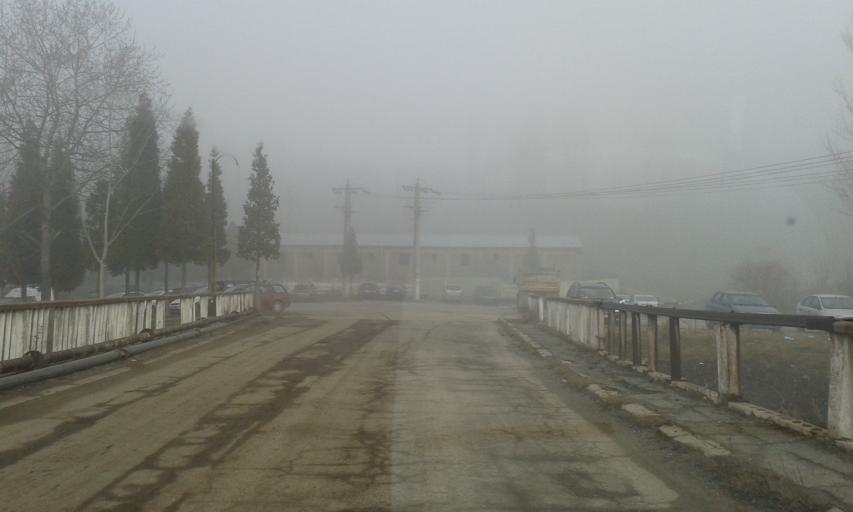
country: RO
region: Hunedoara
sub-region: Municipiul  Vulcan
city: Jiu-Paroseni
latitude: 45.3683
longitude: 23.2657
